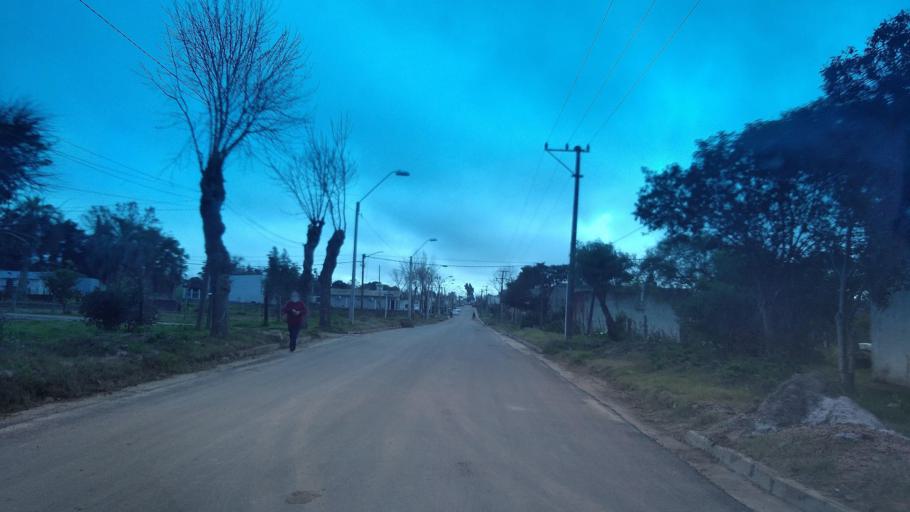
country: UY
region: Canelones
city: Tala
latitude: -34.1999
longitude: -55.7405
